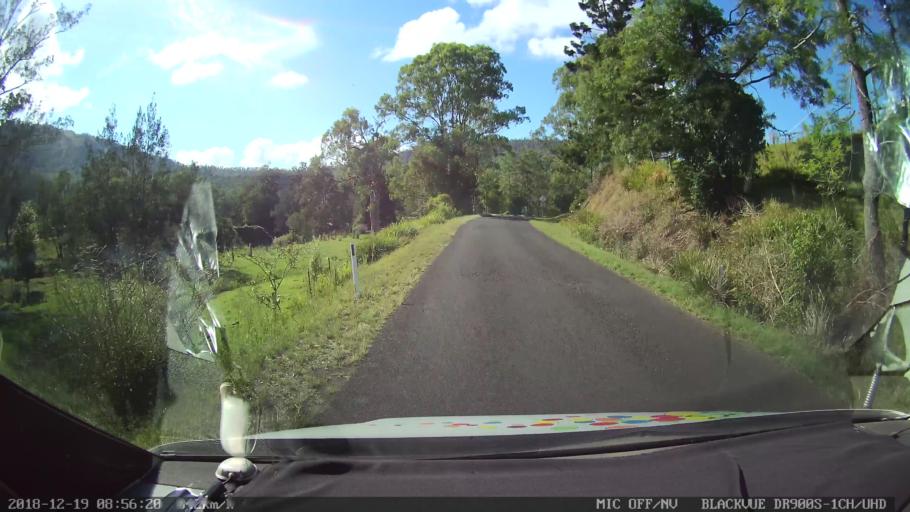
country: AU
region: New South Wales
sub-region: Kyogle
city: Kyogle
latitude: -28.4182
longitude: 152.9763
